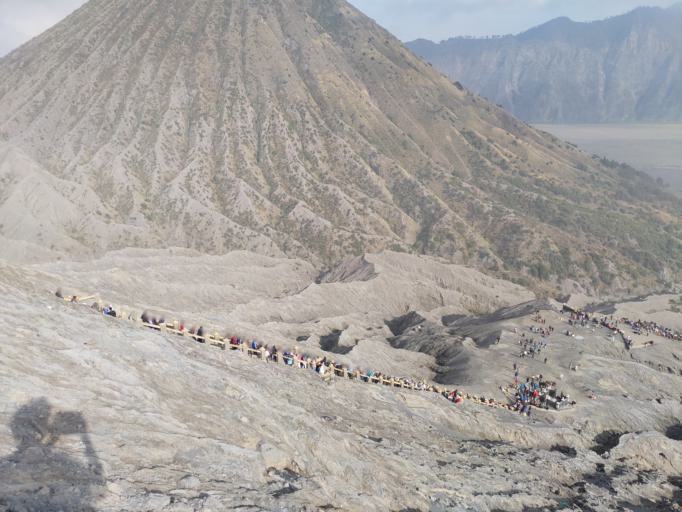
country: ID
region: East Java
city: Gubugklakah Barat
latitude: -7.9401
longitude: 112.9531
